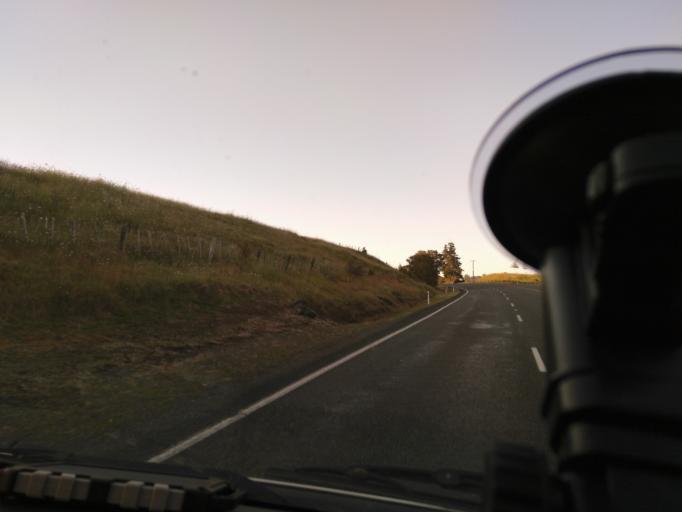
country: NZ
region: Northland
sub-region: Far North District
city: Taipa
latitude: -35.0482
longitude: 173.6705
